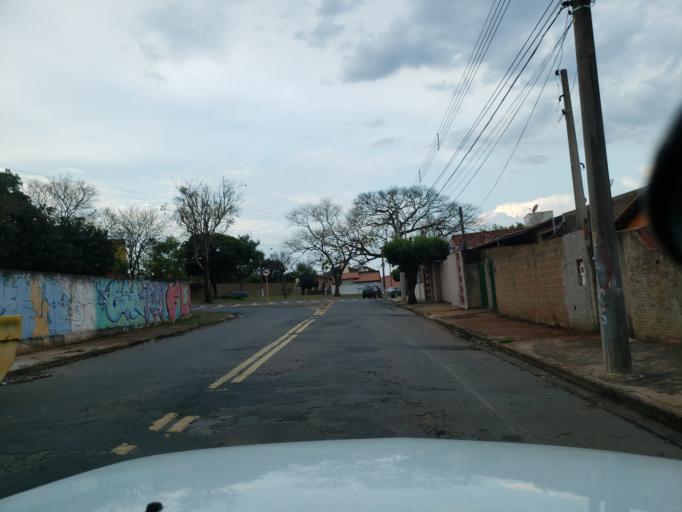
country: BR
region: Sao Paulo
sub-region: Moji-Guacu
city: Mogi-Gaucu
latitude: -22.3618
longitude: -46.9405
